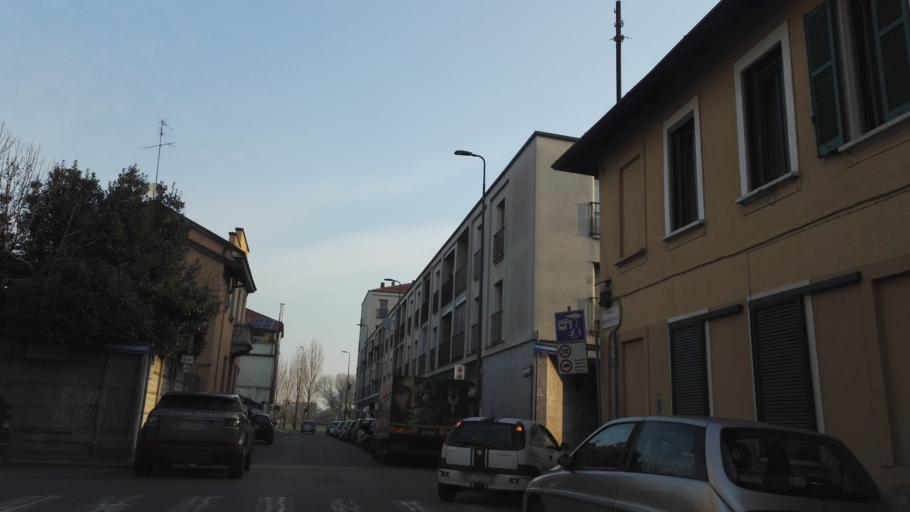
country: IT
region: Lombardy
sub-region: Citta metropolitana di Milano
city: Linate
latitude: 45.4435
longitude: 9.2640
